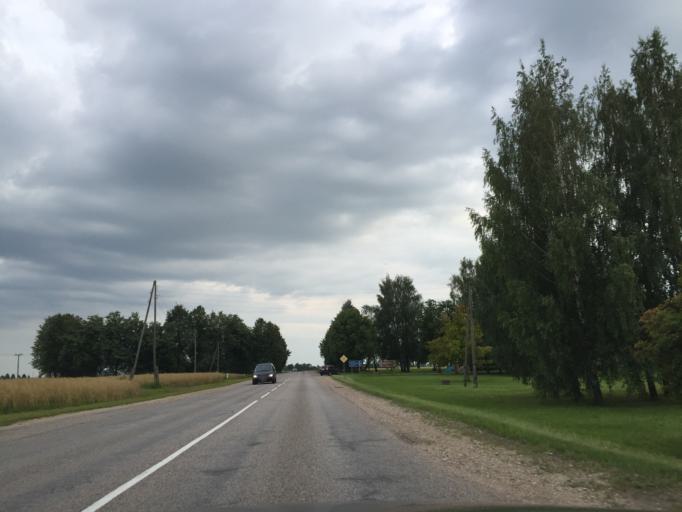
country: LV
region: Dobeles Rajons
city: Dobele
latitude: 56.5674
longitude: 23.3005
